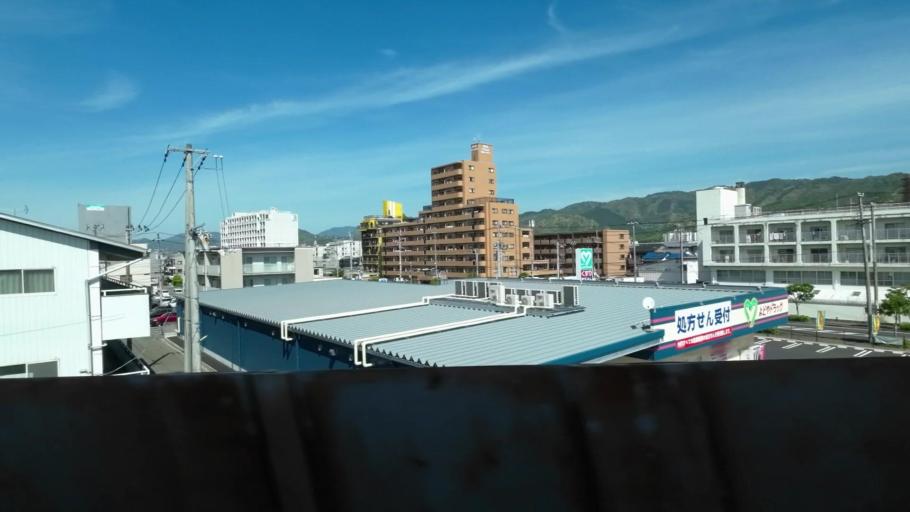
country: JP
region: Kochi
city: Kochi-shi
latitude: 33.5691
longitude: 133.5523
